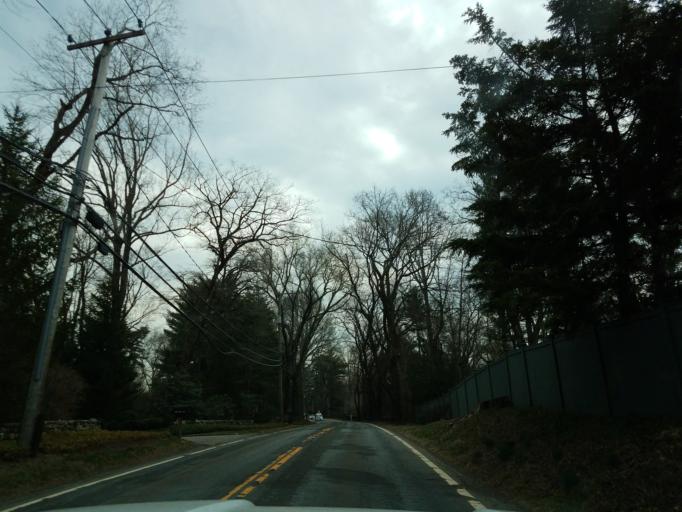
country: US
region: Connecticut
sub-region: Fairfield County
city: Glenville
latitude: 41.0563
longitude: -73.6393
